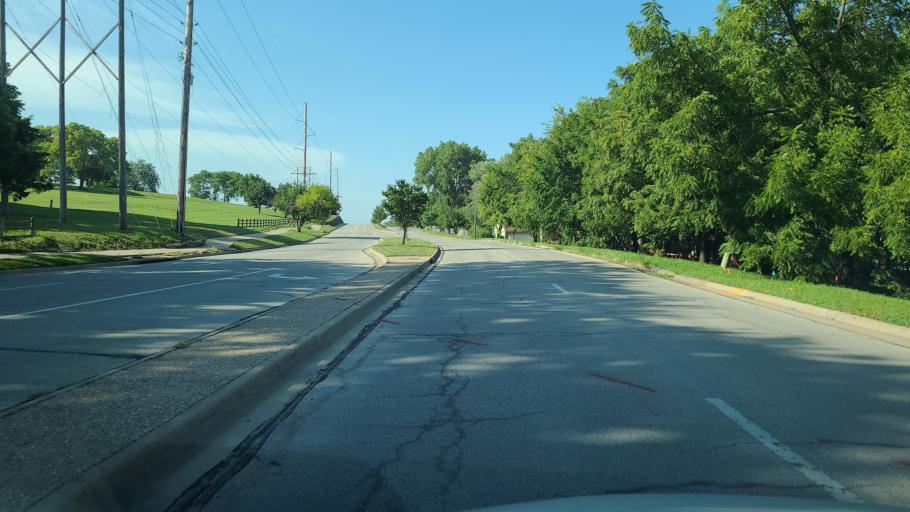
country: US
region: Kansas
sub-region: Douglas County
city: Lawrence
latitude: 38.9817
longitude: -95.2790
